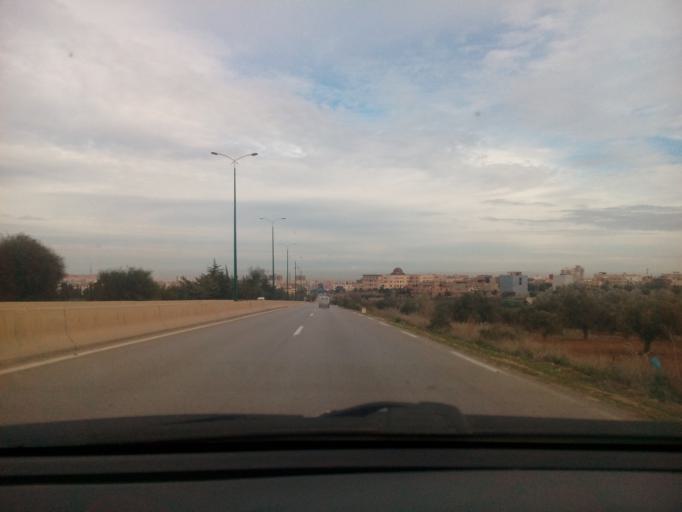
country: DZ
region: Tlemcen
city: Mansoura
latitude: 34.8723
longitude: -1.3496
